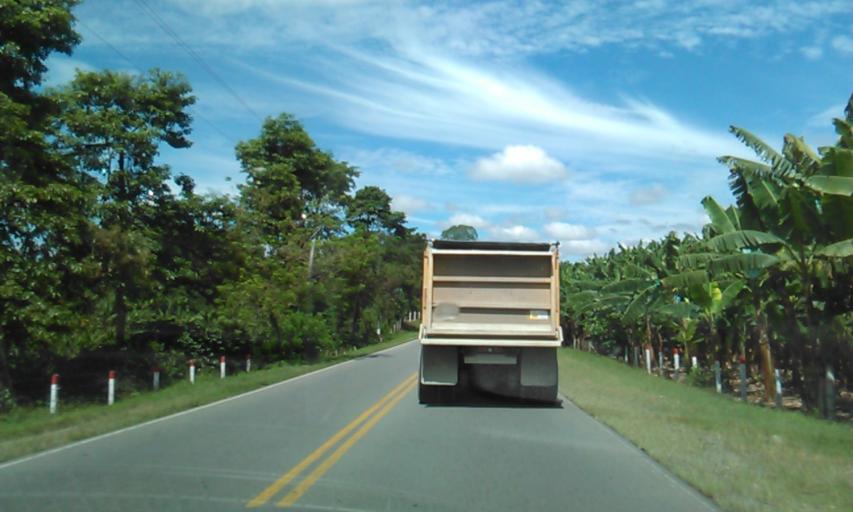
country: CO
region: Quindio
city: Cordoba
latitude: 4.4398
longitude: -75.7178
